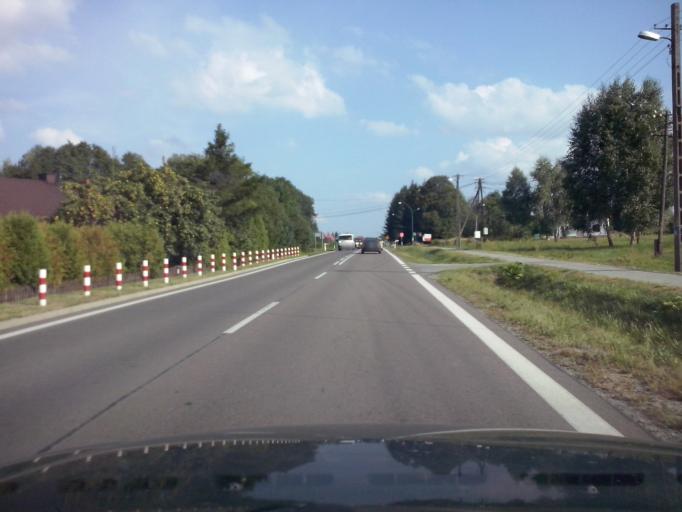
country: PL
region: Subcarpathian Voivodeship
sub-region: Powiat kolbuszowski
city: Niwiska
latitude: 50.2648
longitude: 21.6500
